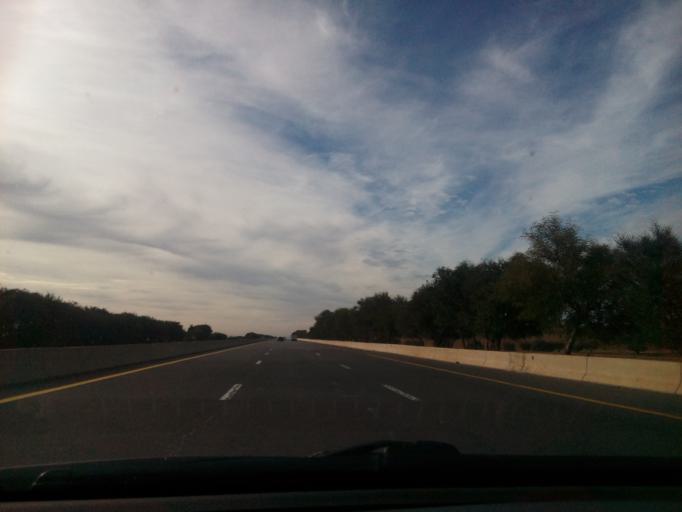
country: DZ
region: Sidi Bel Abbes
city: Sidi Bel Abbes
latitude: 35.2066
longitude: -0.6878
